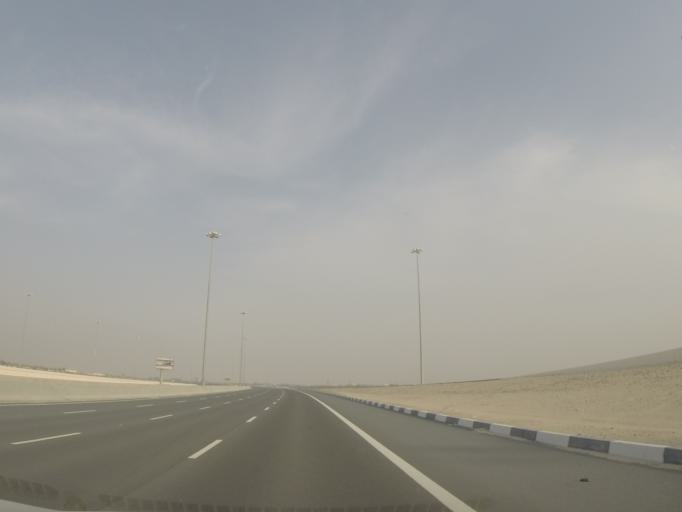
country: AE
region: Abu Dhabi
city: Abu Dhabi
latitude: 24.7049
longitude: 54.7553
